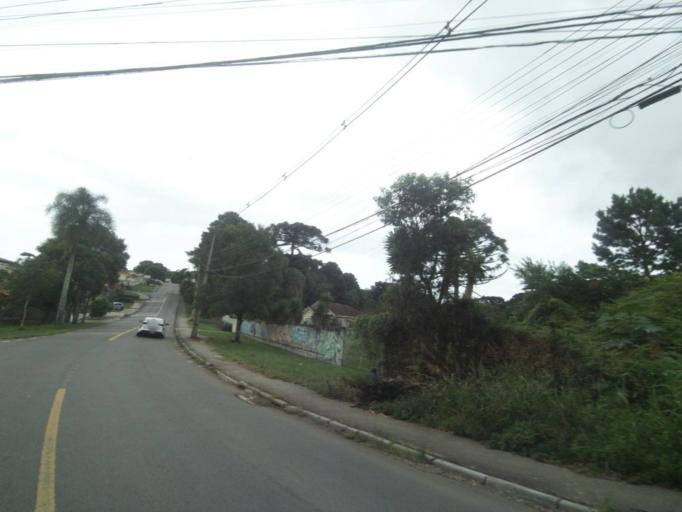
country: BR
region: Parana
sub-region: Curitiba
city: Curitiba
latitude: -25.4538
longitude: -49.3241
